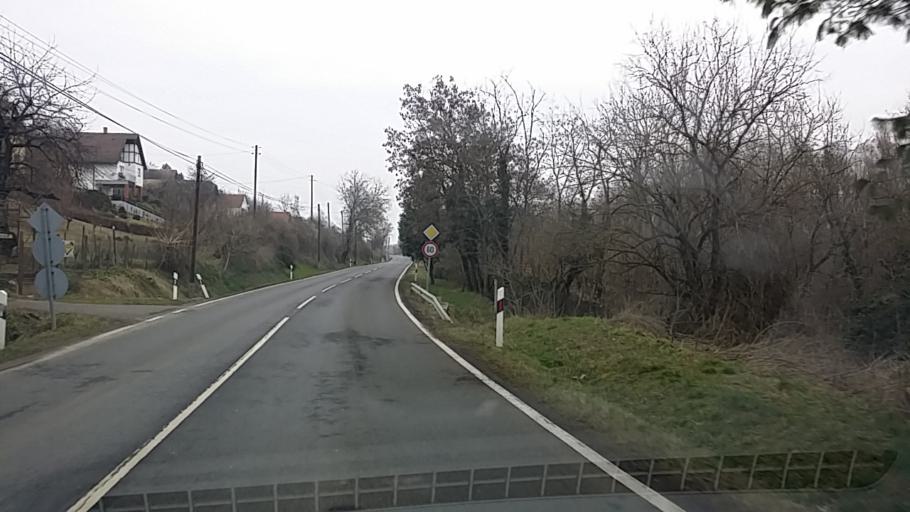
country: HU
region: Baranya
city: Mohacs
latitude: 46.0421
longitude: 18.7084
